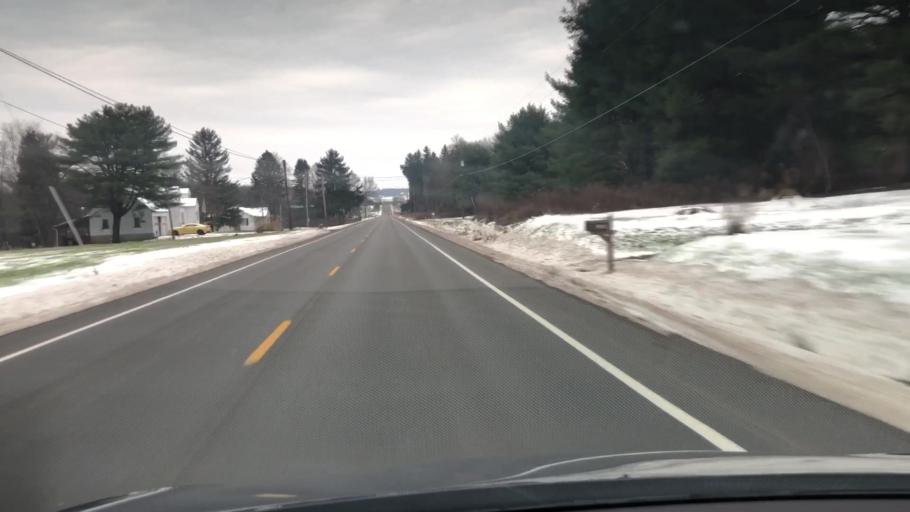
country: US
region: Pennsylvania
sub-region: Jefferson County
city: Brookville
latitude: 41.0925
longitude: -79.2261
